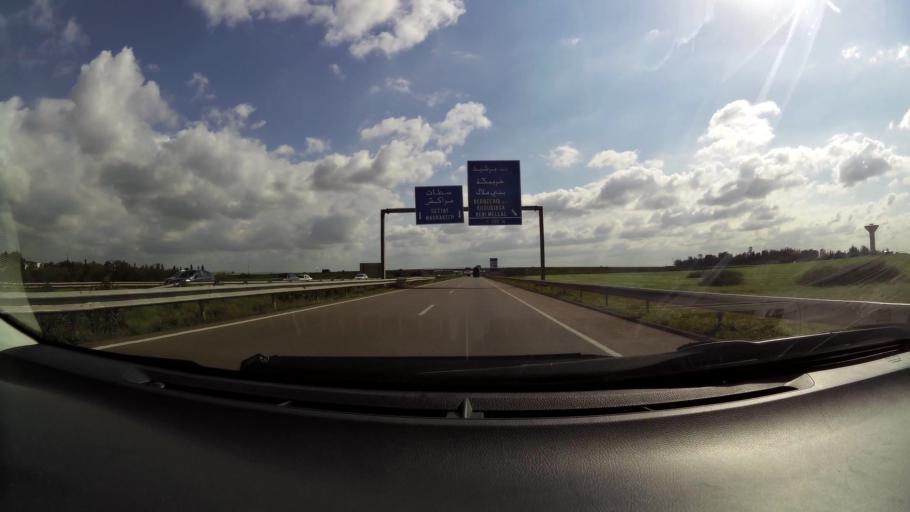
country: MA
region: Chaouia-Ouardigha
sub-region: Settat Province
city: Berrechid
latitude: 33.2526
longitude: -7.5610
